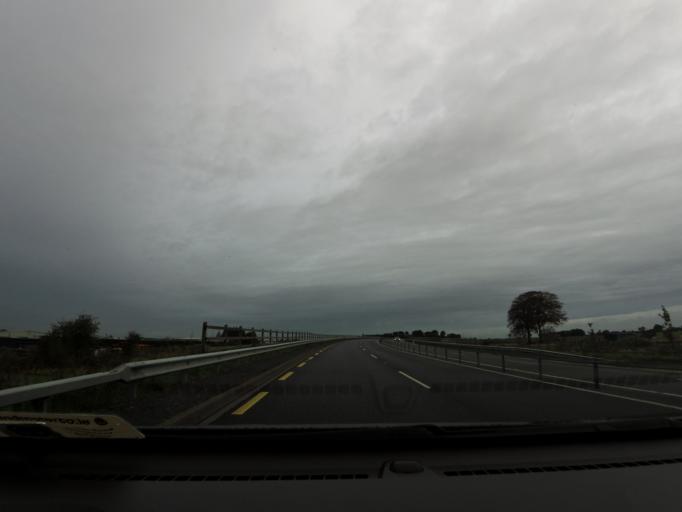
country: IE
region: Connaught
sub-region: County Galway
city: Tuam
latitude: 53.5182
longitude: -8.8778
